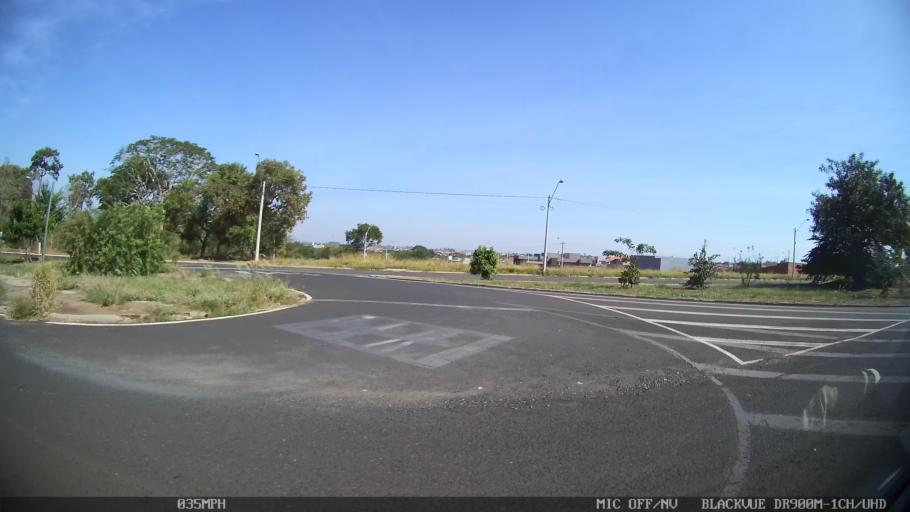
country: BR
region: Sao Paulo
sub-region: Sao Jose Do Rio Preto
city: Sao Jose do Rio Preto
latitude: -20.7841
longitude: -49.4263
